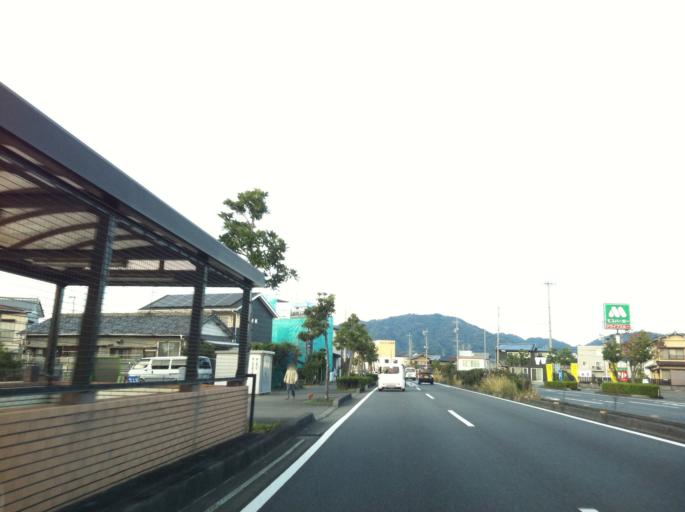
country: JP
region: Shizuoka
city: Yaizu
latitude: 34.8573
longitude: 138.3007
